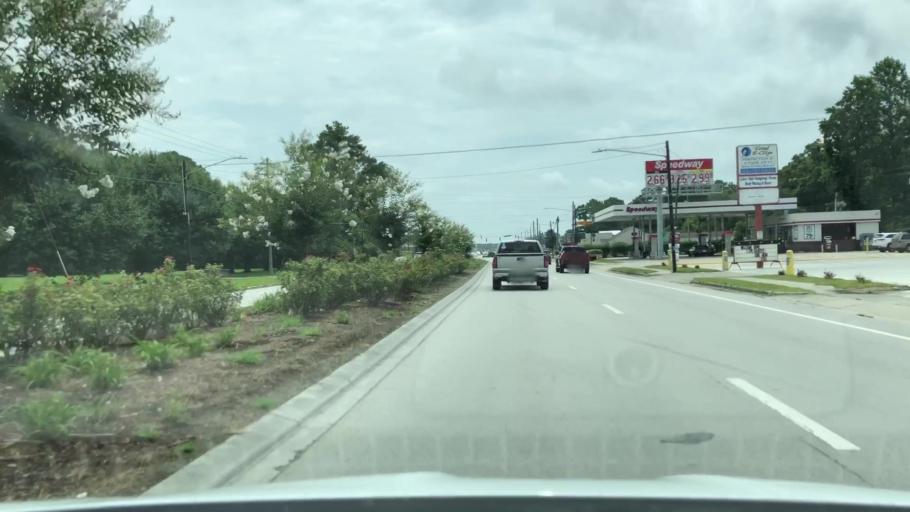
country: US
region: North Carolina
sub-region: Craven County
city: Havelock
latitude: 34.8729
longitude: -76.9024
